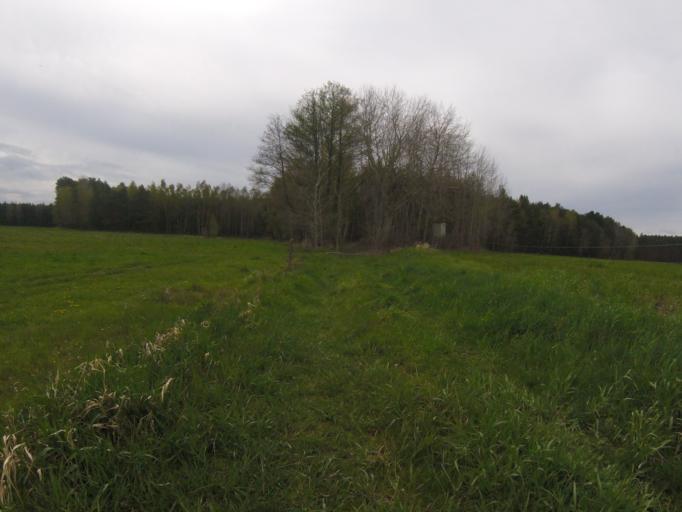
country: DE
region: Brandenburg
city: Bestensee
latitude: 52.2207
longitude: 13.6910
